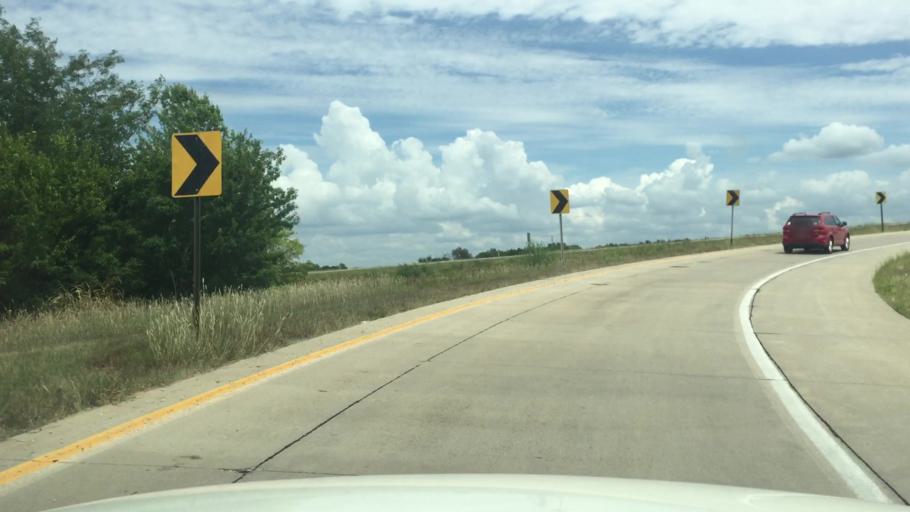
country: US
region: Kansas
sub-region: Shawnee County
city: Topeka
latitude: 39.0465
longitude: -95.6036
